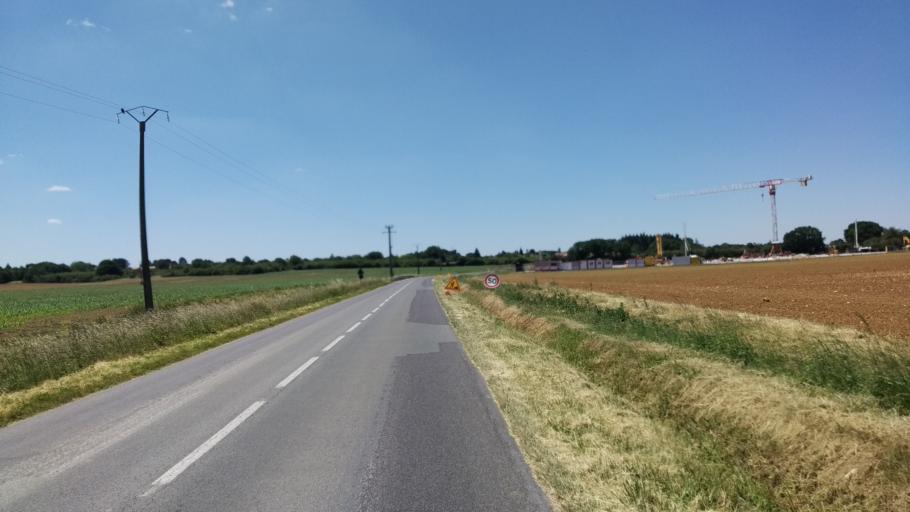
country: FR
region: Poitou-Charentes
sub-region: Departement de la Vienne
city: Biard
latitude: 46.5991
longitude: 0.2941
